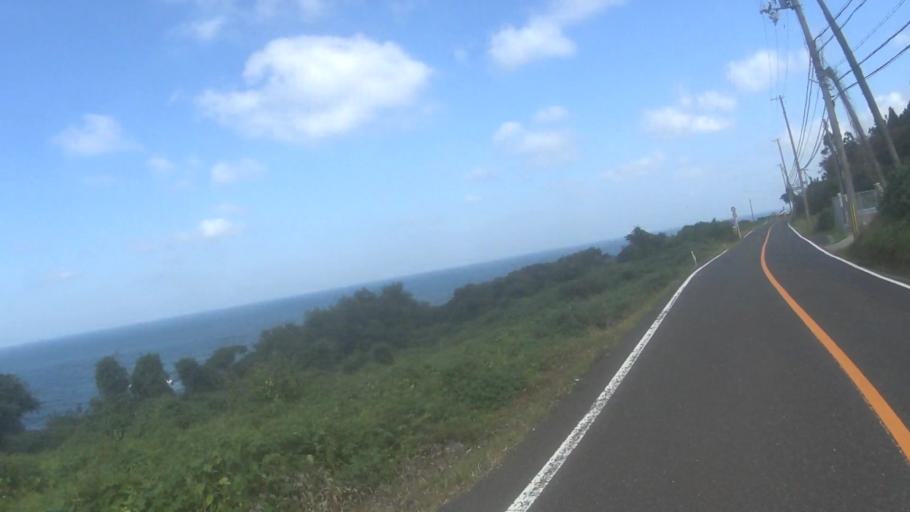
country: JP
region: Kyoto
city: Miyazu
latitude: 35.7501
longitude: 135.1503
